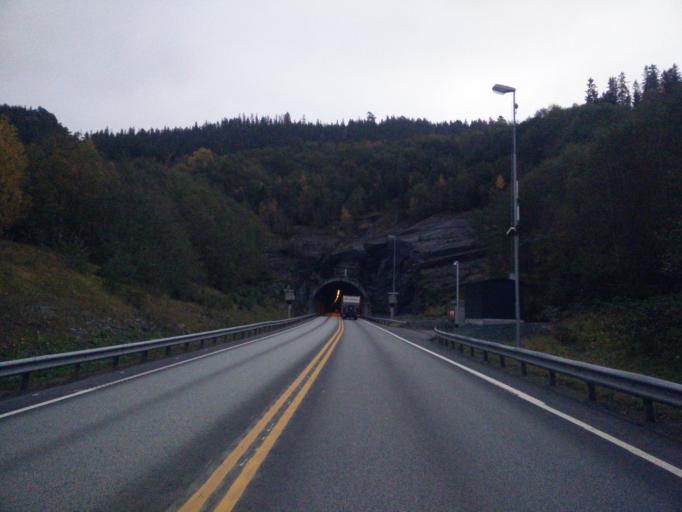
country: NO
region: Sor-Trondelag
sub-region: Malvik
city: Malvik
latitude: 63.4231
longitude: 10.5813
